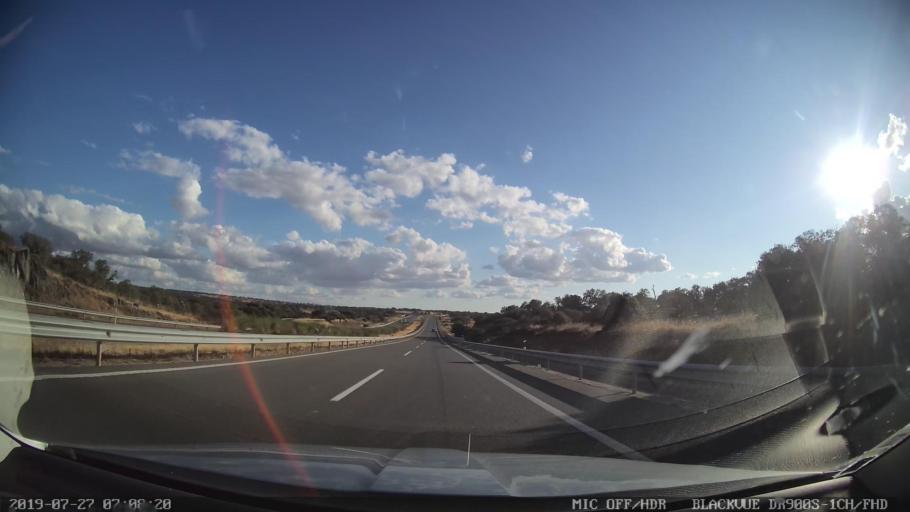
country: ES
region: Extremadura
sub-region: Provincia de Caceres
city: Jaraicejo
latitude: 39.6144
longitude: -5.8316
